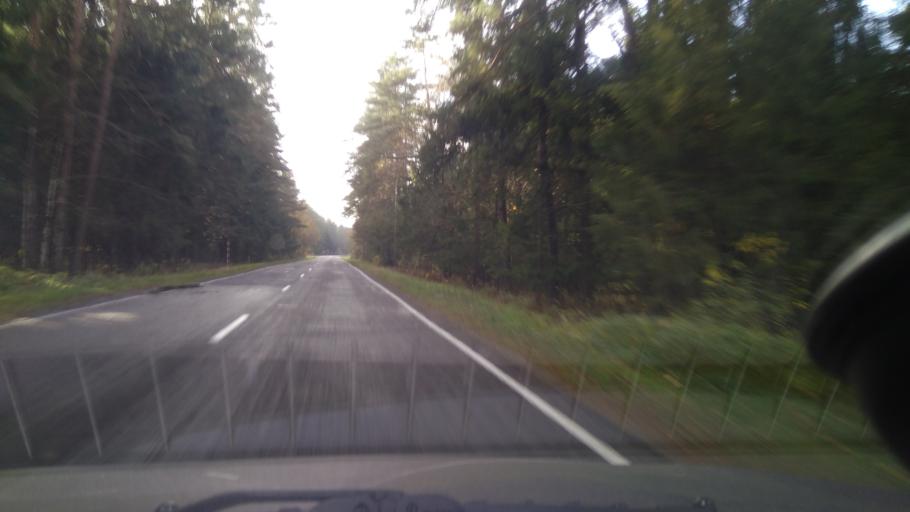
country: BY
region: Minsk
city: Slutsk
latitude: 53.2249
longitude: 27.6086
